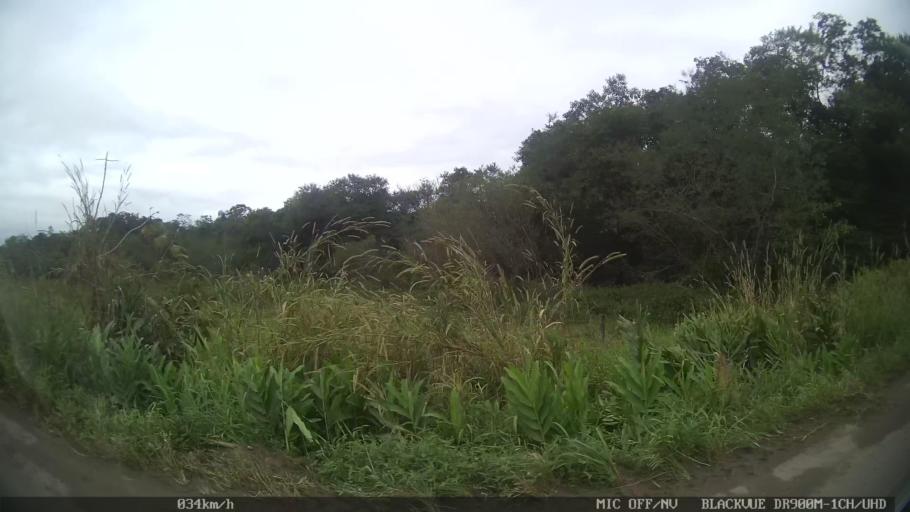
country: BR
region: Santa Catarina
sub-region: Joinville
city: Joinville
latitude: -26.2684
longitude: -48.9229
